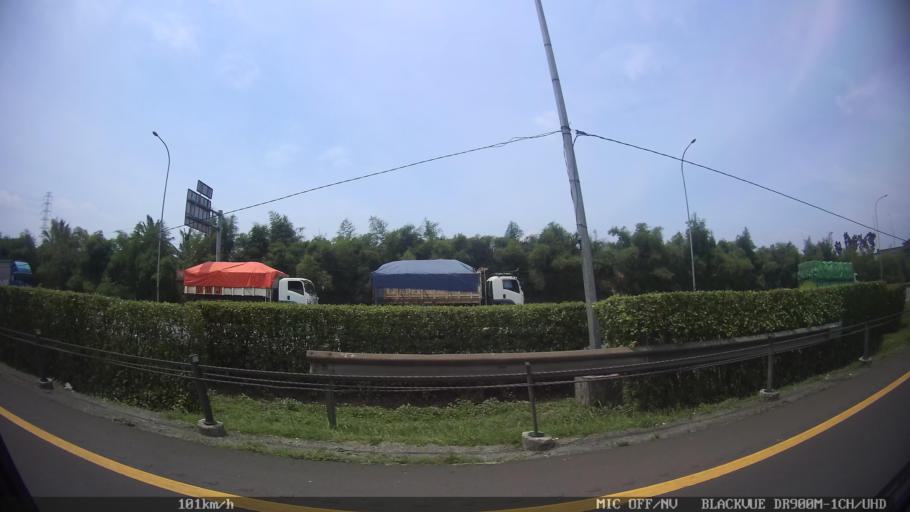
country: ID
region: West Java
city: Kresek
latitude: -6.1721
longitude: 106.3462
